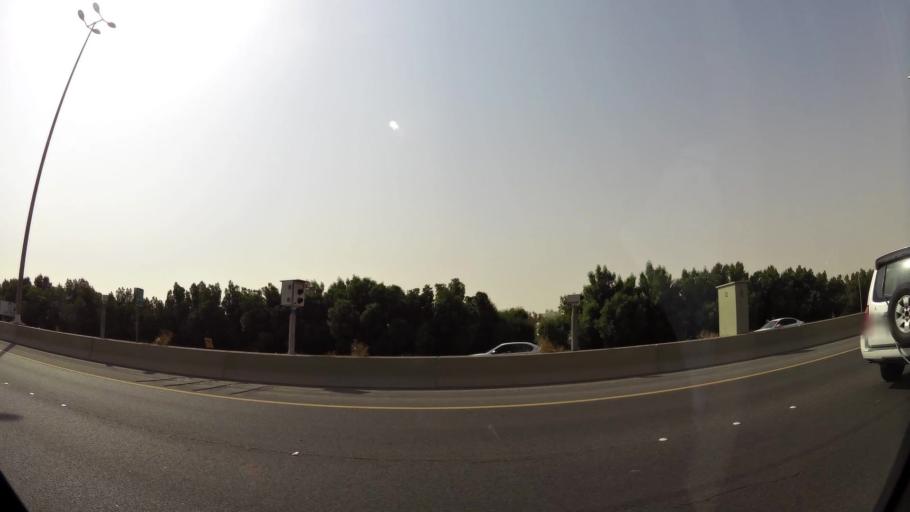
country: KW
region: Muhafazat al Jahra'
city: Al Jahra'
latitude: 29.3452
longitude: 47.7036
